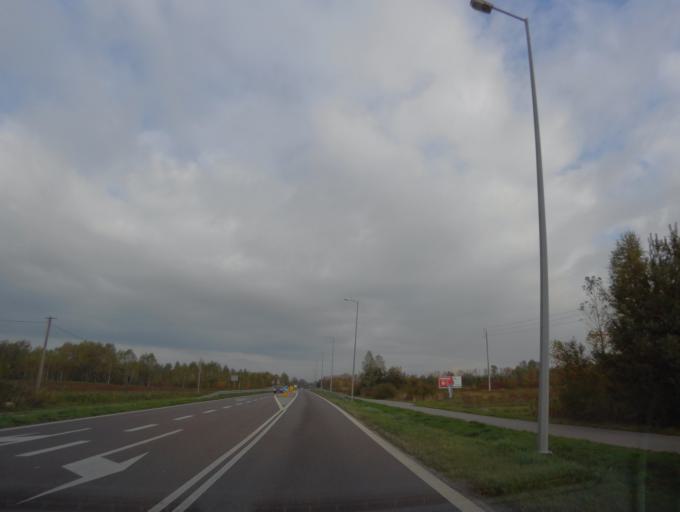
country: PL
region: Lublin Voivodeship
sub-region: Powiat bilgorajski
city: Frampol
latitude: 50.6557
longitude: 22.6818
